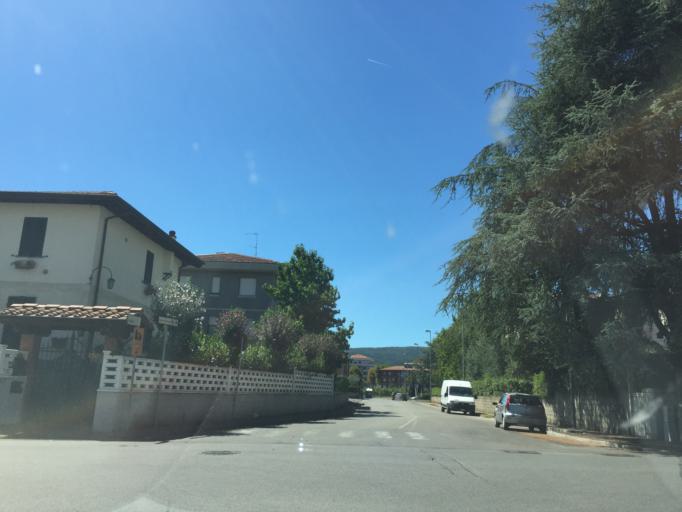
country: IT
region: Tuscany
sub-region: Provincia di Pistoia
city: Pistoia
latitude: 43.9486
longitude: 10.9048
